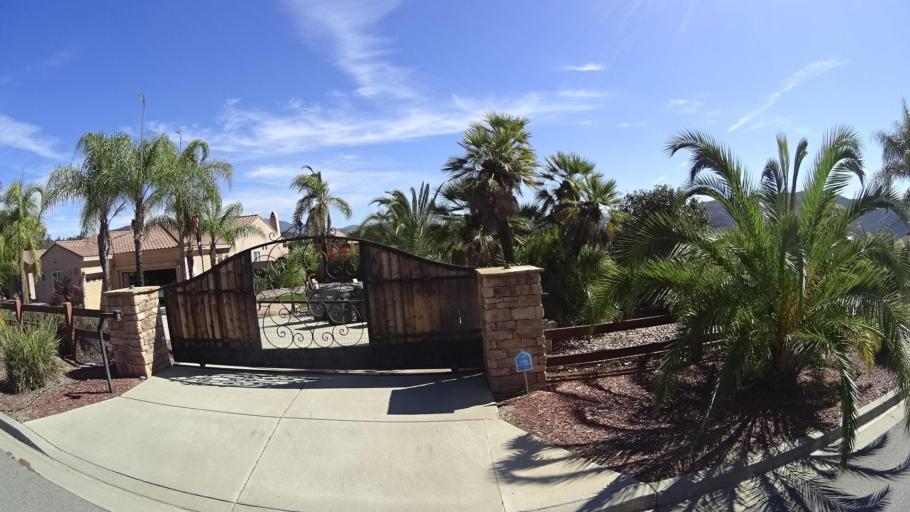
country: US
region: California
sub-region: San Diego County
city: Harbison Canyon
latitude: 32.8727
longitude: -116.8419
